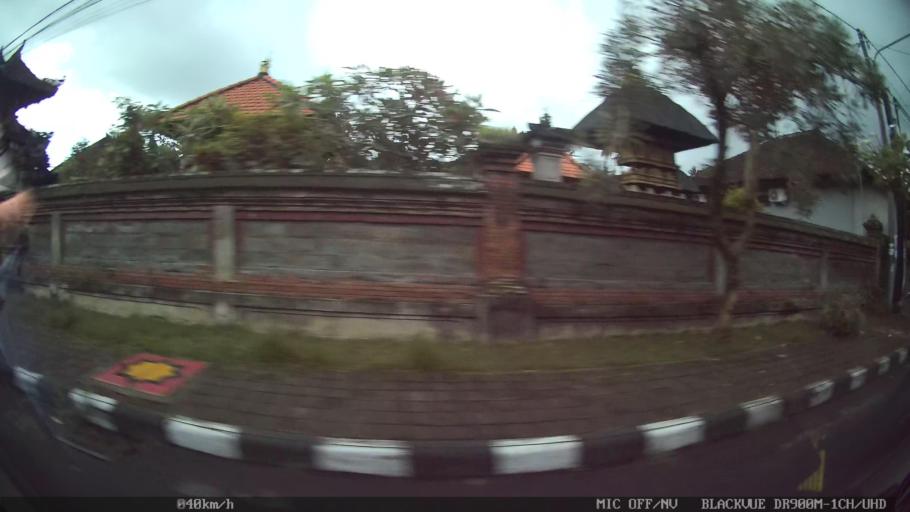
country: ID
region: Bali
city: Banjar Sempidi
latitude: -8.5155
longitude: 115.2056
